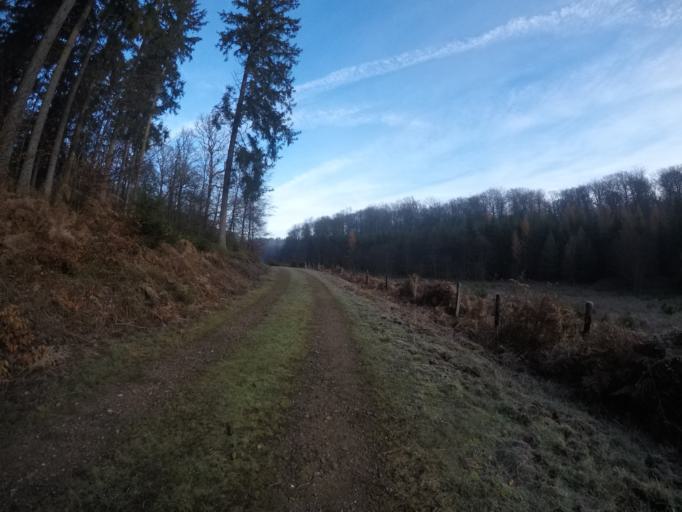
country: BE
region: Wallonia
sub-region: Province du Luxembourg
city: Habay-la-Vieille
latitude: 49.7596
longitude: 5.6602
